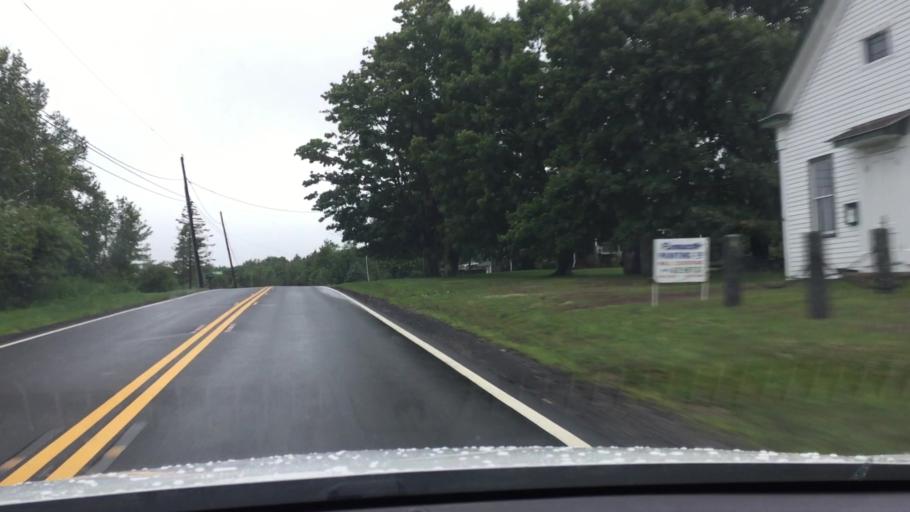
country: US
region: Massachusetts
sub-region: Berkshire County
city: Becket
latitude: 42.3654
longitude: -73.1428
